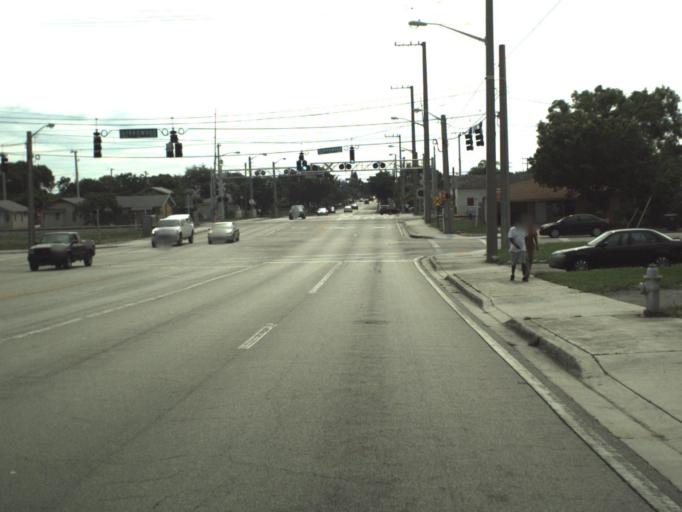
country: US
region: Florida
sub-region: Palm Beach County
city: Mangonia Park
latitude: 26.7530
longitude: -80.0614
